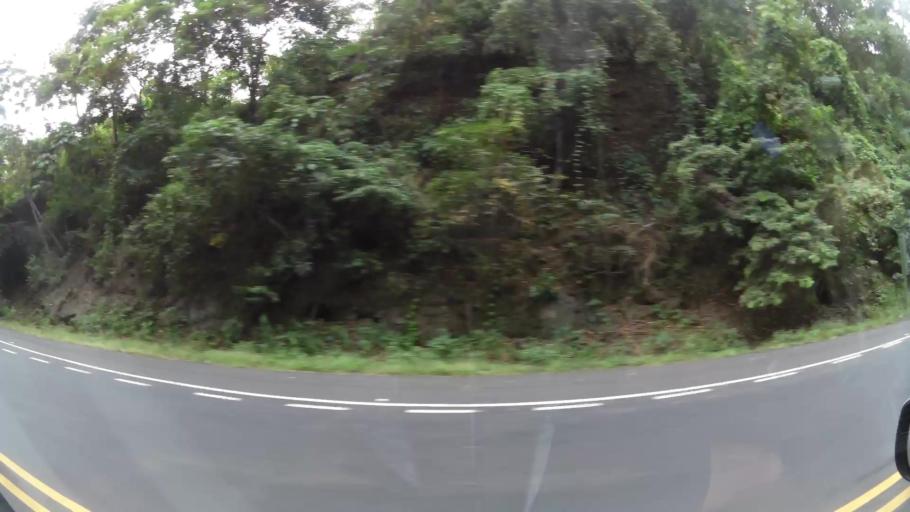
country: CR
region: Puntarenas
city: Esparza
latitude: 9.9087
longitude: -84.6695
